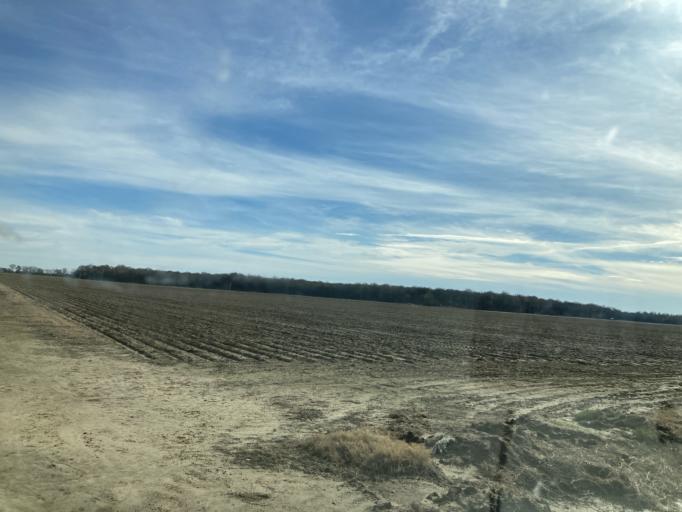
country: US
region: Mississippi
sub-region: Humphreys County
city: Belzoni
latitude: 33.0665
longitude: -90.6340
